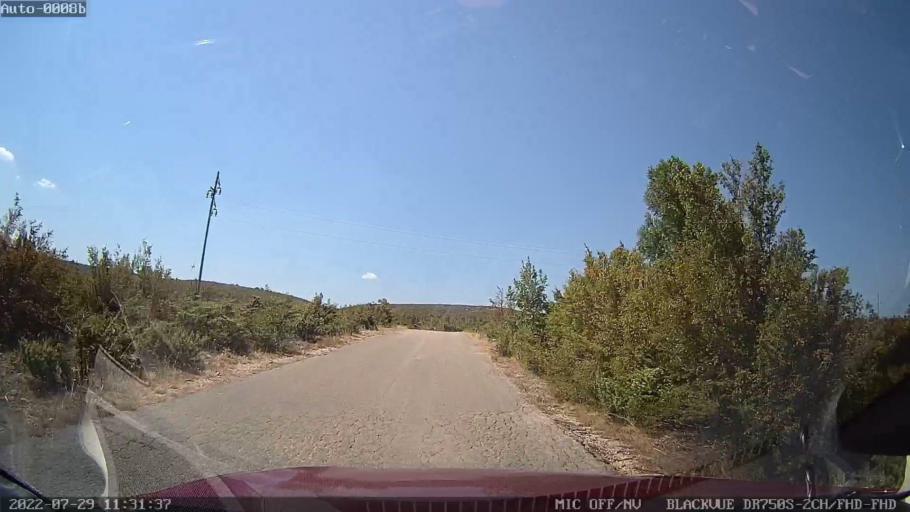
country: HR
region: Zadarska
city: Obrovac
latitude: 44.1960
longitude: 15.7457
